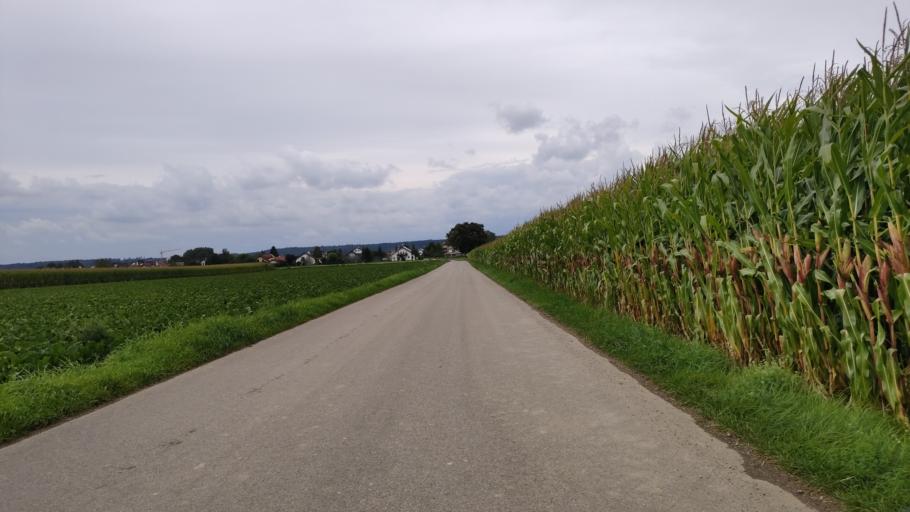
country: DE
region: Bavaria
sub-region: Swabia
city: Wehringen
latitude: 48.2414
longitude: 10.8084
